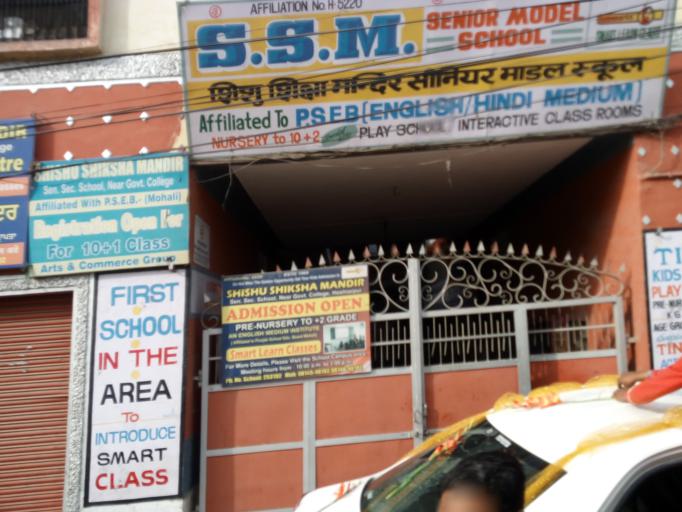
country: IN
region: Punjab
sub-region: Hoshiarpur
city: Hoshiarpur
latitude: 31.5275
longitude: 75.9003
